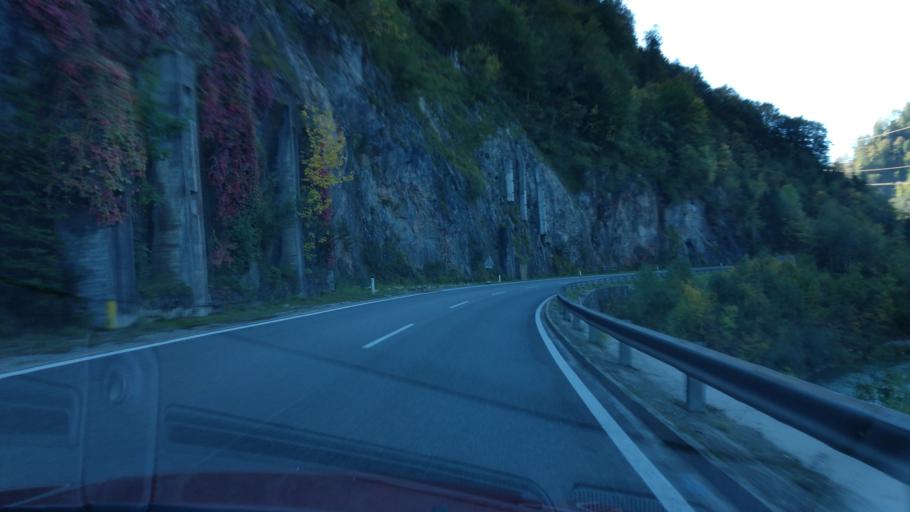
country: AT
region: Styria
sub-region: Politischer Bezirk Liezen
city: Altenmarkt bei Sankt Gallen
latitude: 47.7782
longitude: 14.6538
